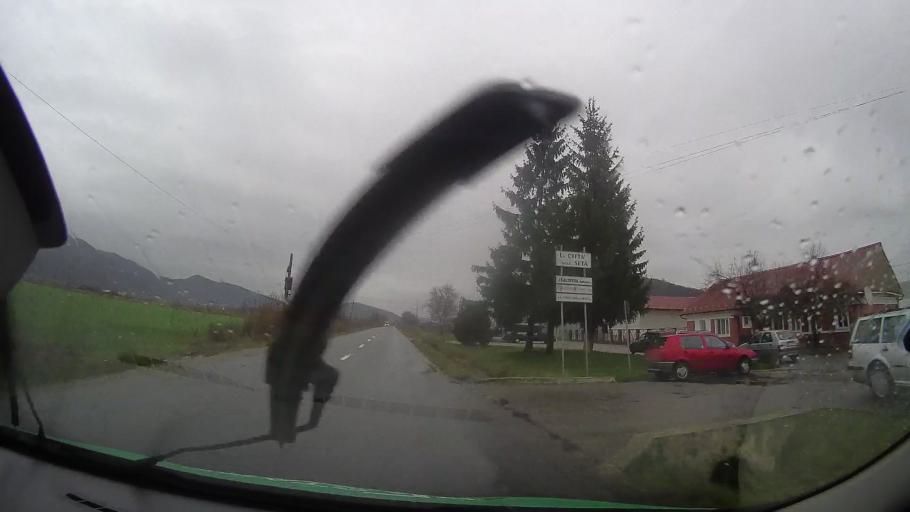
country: RO
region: Bistrita-Nasaud
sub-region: Municipiul Bistrita
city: Viisoara
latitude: 47.0614
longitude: 24.4363
